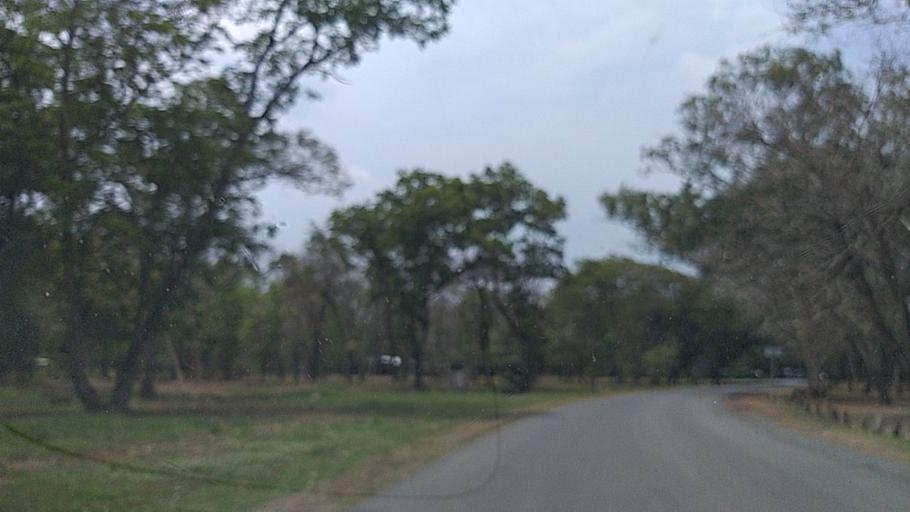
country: TH
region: Bangkok
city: Thawi Watthana
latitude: 13.7710
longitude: 100.3138
